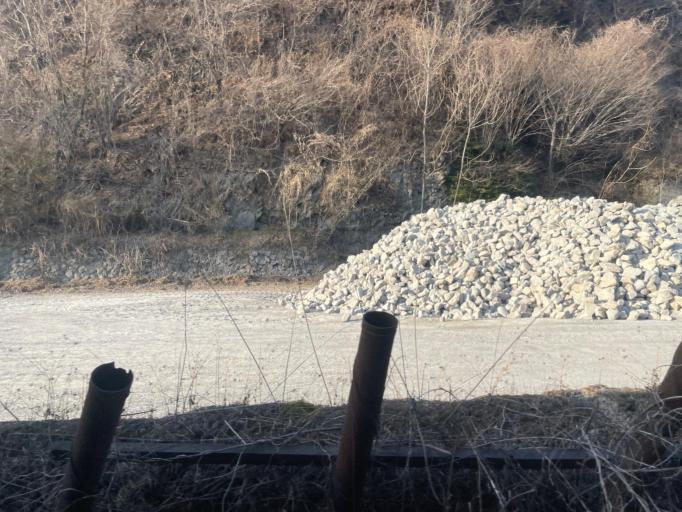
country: JP
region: Gunma
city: Nakanojomachi
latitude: 36.5525
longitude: 138.9247
